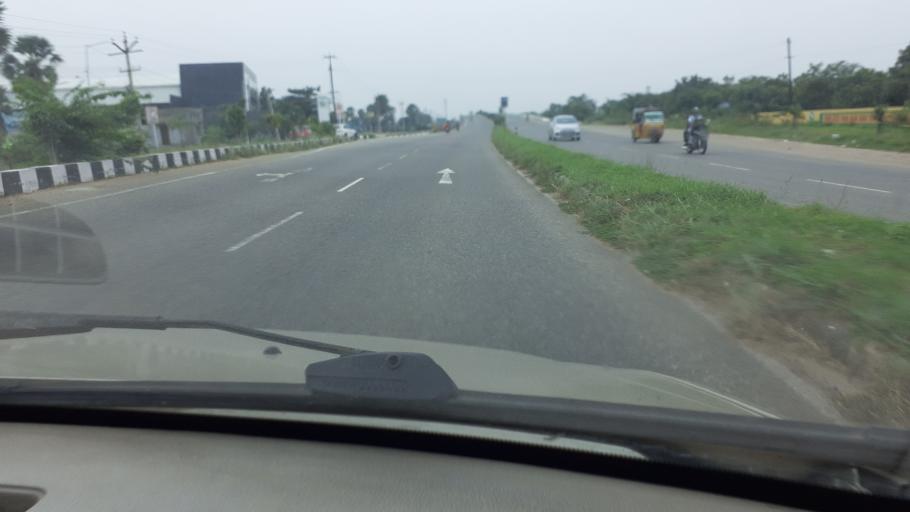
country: IN
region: Tamil Nadu
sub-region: Tirunelveli Kattabo
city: Tirunelveli
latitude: 8.6452
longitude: 77.7081
